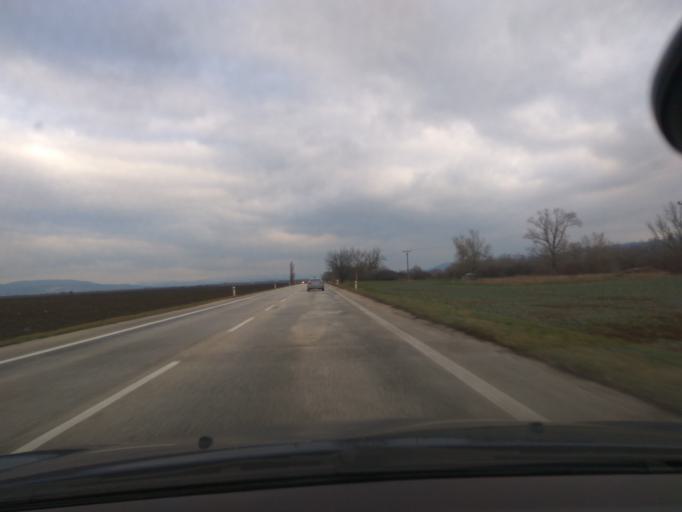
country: SK
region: Trnavsky
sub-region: Okres Trnava
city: Piestany
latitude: 48.6208
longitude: 17.8370
